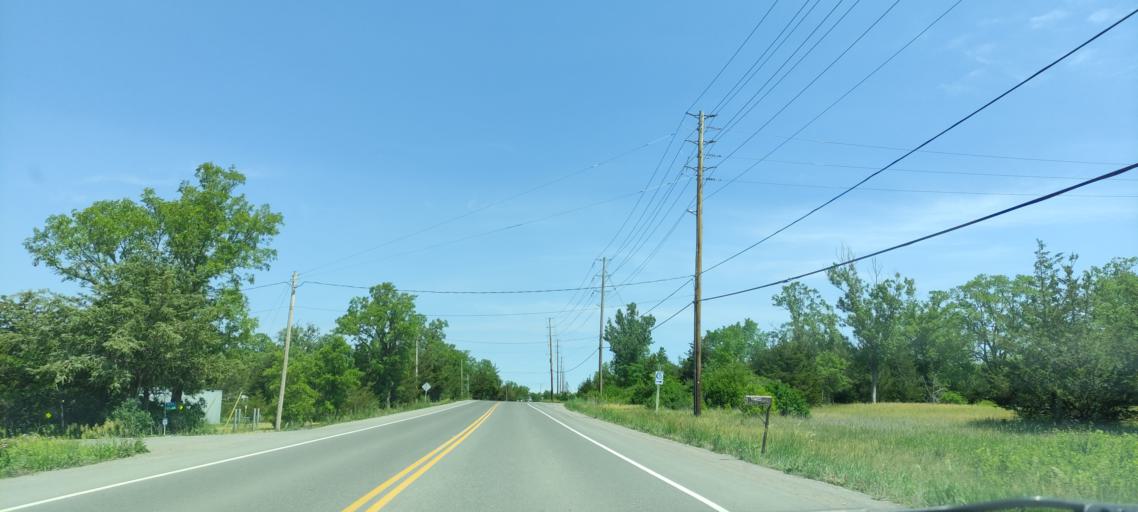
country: CA
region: Ontario
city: Quinte West
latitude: 44.2753
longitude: -77.8104
